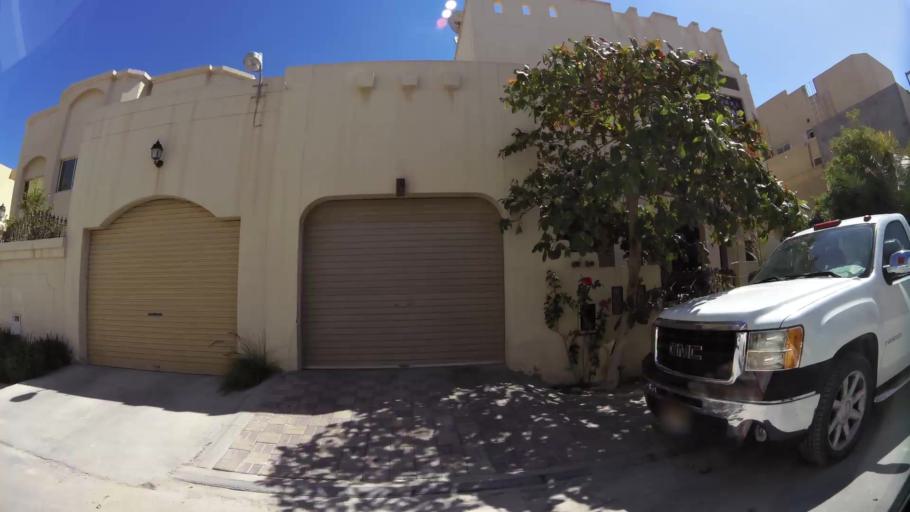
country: BH
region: Muharraq
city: Al Muharraq
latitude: 26.2803
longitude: 50.6024
